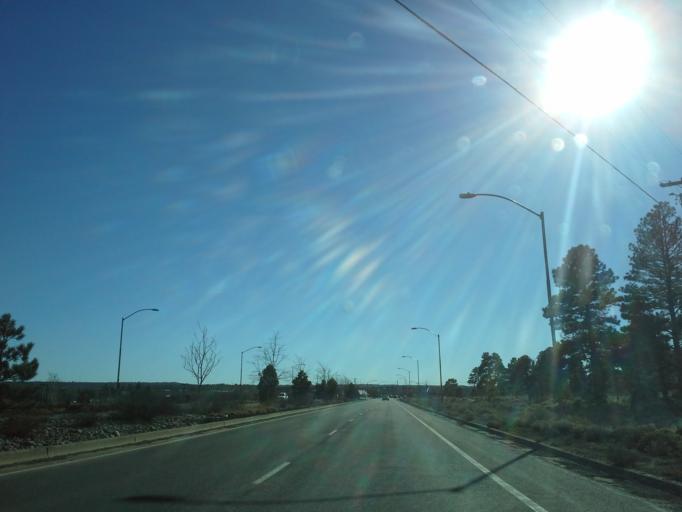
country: US
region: Arizona
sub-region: Coconino County
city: Flagstaff
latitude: 35.2293
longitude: -111.5789
